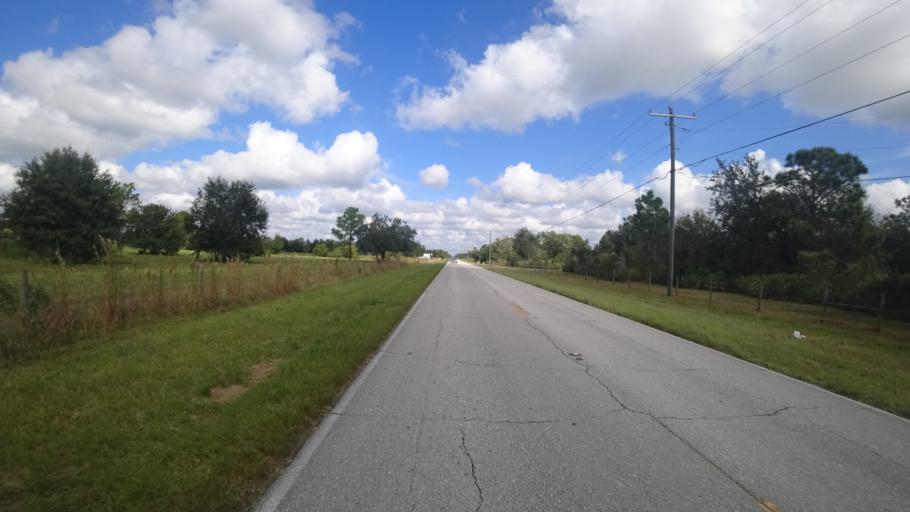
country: US
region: Florida
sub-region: Sarasota County
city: Lake Sarasota
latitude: 27.3987
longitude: -82.2711
